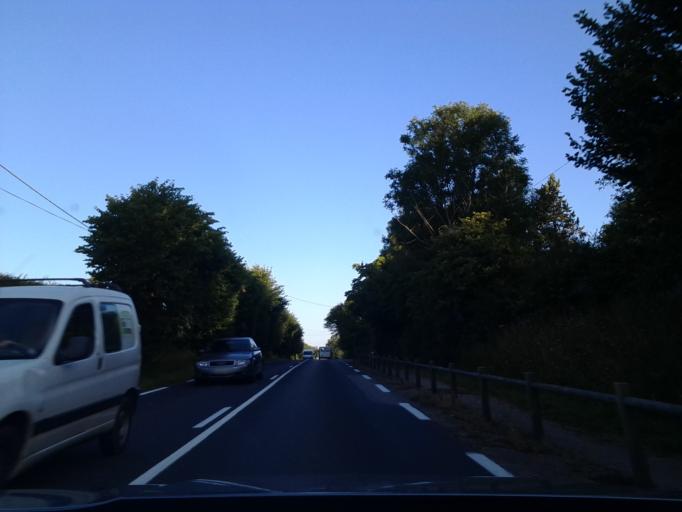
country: FR
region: Lower Normandy
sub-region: Departement de la Manche
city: Valognes
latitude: 49.5155
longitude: -1.4867
